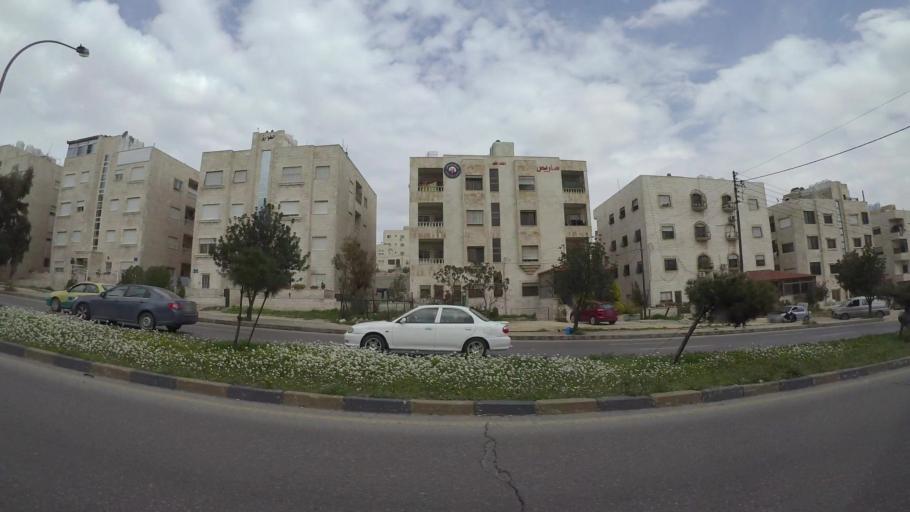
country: JO
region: Amman
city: Amman
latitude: 31.9689
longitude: 35.9436
